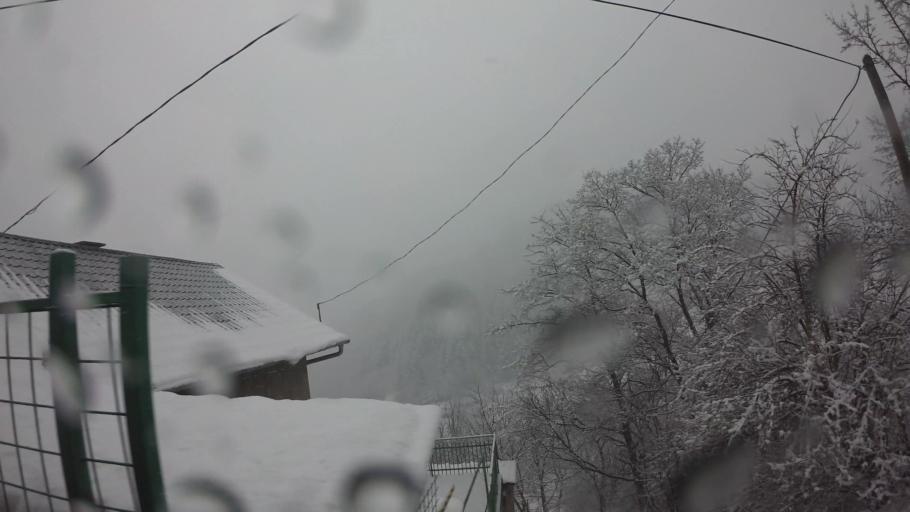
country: BA
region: Federation of Bosnia and Herzegovina
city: Kobilja Glava
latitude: 43.8520
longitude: 18.4510
